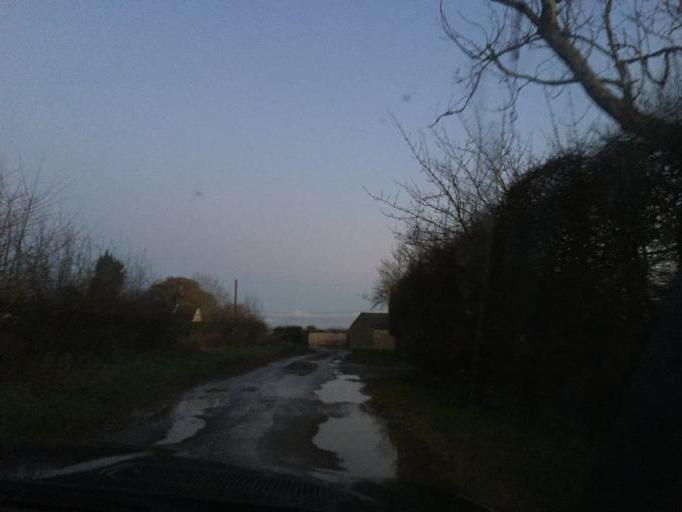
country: GB
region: England
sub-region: Northamptonshire
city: Silverstone
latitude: 52.0887
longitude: -1.0954
